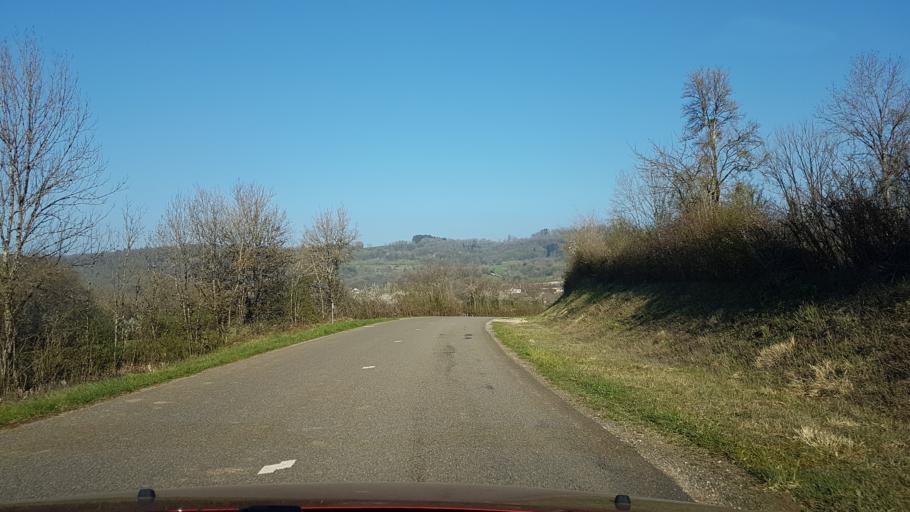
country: FR
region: Bourgogne
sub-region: Departement de Saone-et-Loire
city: Cuiseaux
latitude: 46.4810
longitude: 5.4711
